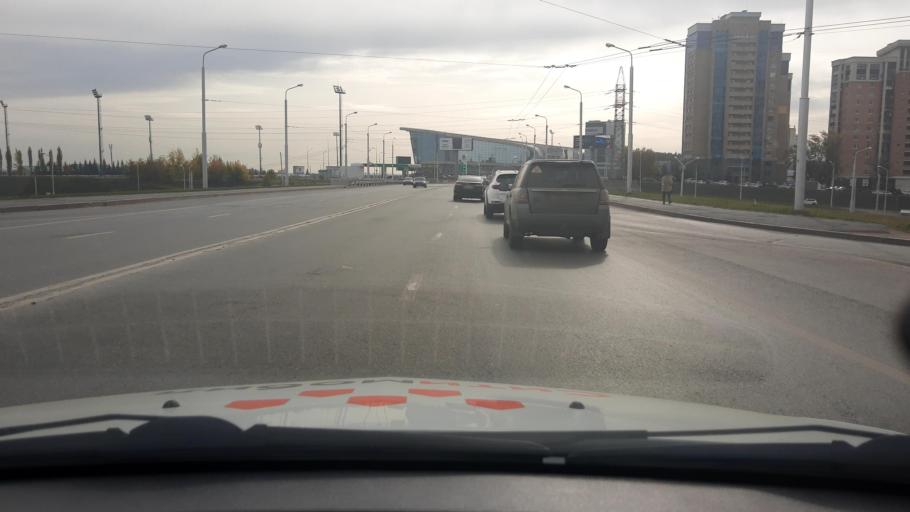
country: RU
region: Bashkortostan
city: Ufa
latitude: 54.7558
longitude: 56.0316
